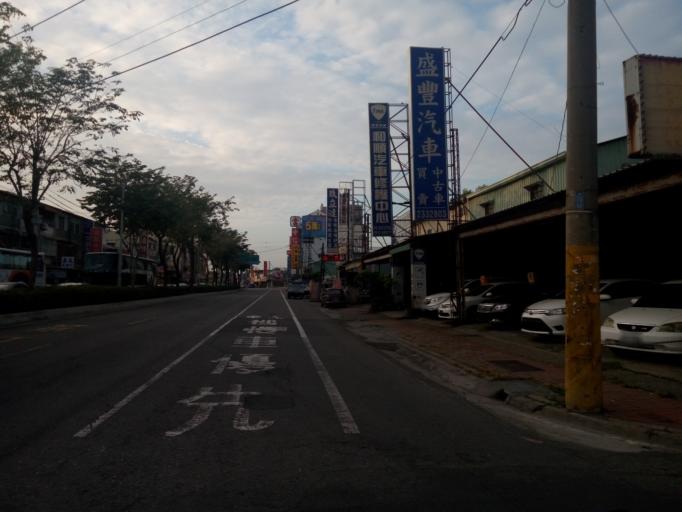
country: TW
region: Taiwan
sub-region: Chiayi
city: Jiayi Shi
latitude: 23.4834
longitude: 120.4246
